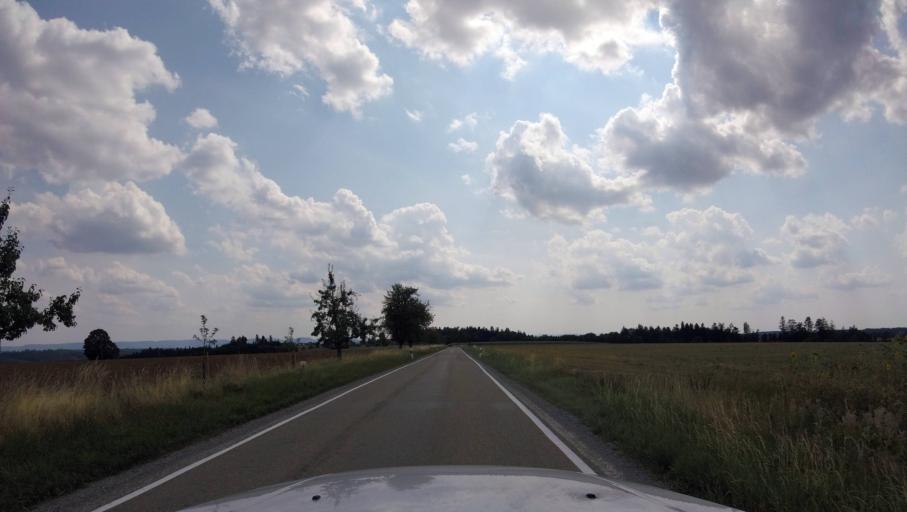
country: DE
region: Baden-Wuerttemberg
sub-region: Regierungsbezirk Stuttgart
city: Spraitbach
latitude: 48.8937
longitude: 9.7247
